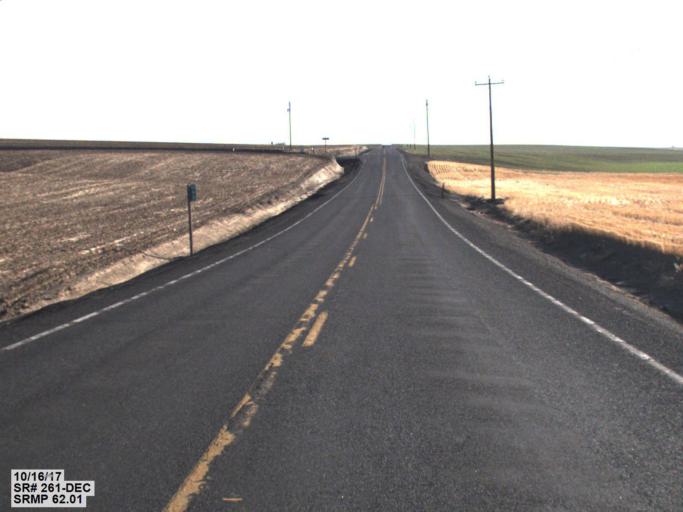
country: US
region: Washington
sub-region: Adams County
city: Ritzville
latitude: 47.1051
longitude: -118.3655
